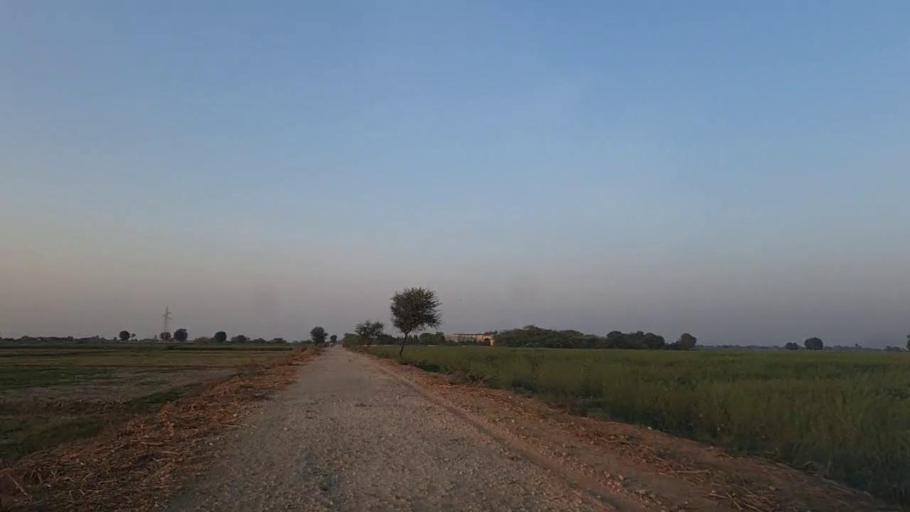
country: PK
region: Sindh
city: Naukot
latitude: 24.9480
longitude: 69.4371
